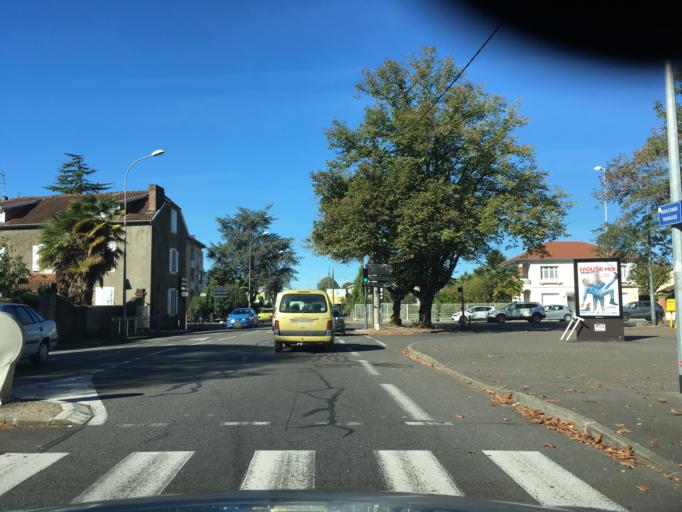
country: FR
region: Aquitaine
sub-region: Departement des Pyrenees-Atlantiques
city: Pau
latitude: 43.3092
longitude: -0.3436
